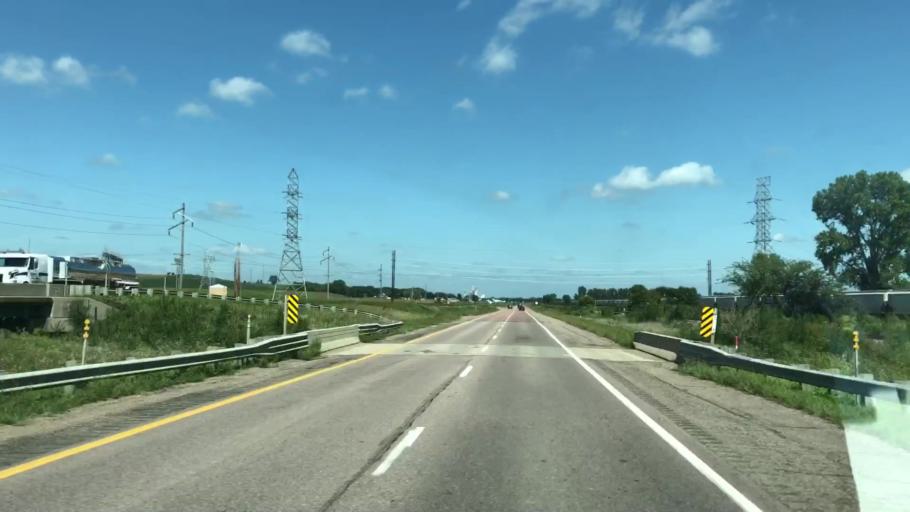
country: US
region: Iowa
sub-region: Woodbury County
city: Sioux City
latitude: 42.5975
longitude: -96.3032
